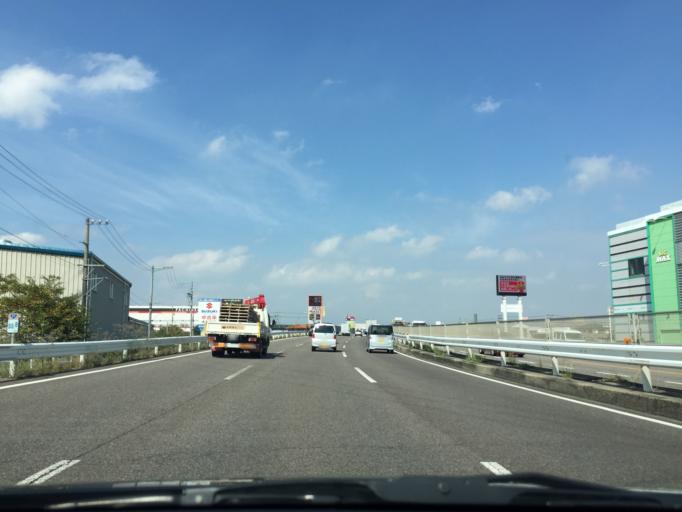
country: JP
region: Gifu
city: Kasamatsucho
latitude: 35.3888
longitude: 136.7437
